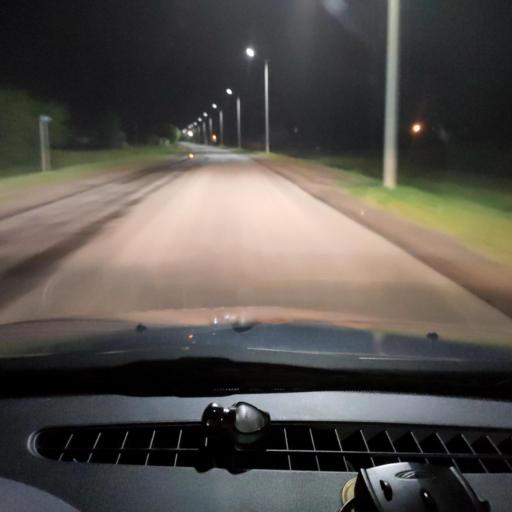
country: RU
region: Voronezj
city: Khrenovoye
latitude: 51.1157
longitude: 40.2646
